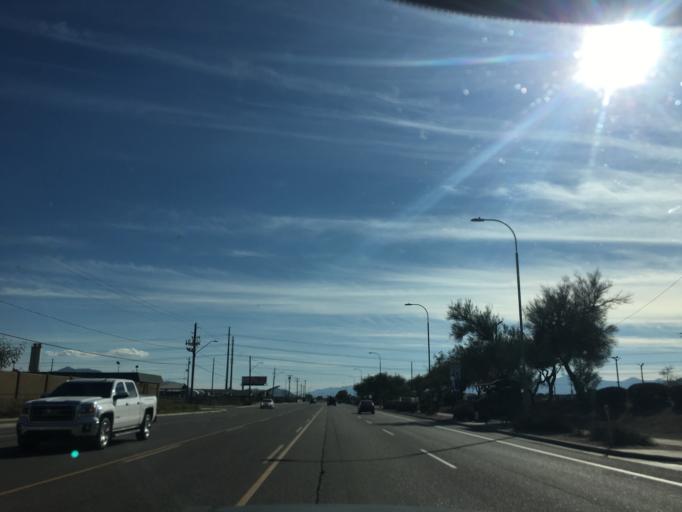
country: US
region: Arizona
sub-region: Maricopa County
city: Laveen
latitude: 33.4184
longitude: -112.1694
